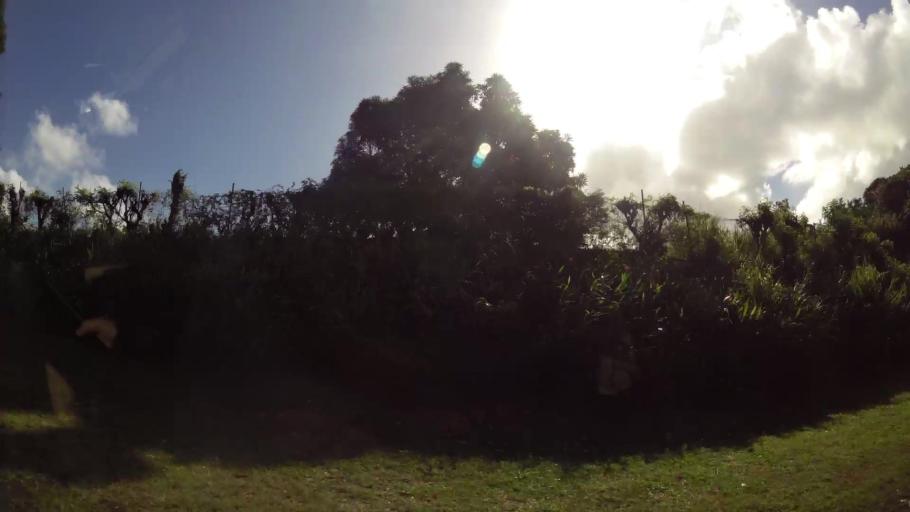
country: MQ
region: Martinique
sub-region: Martinique
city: Sainte-Marie
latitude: 14.7744
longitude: -60.9904
